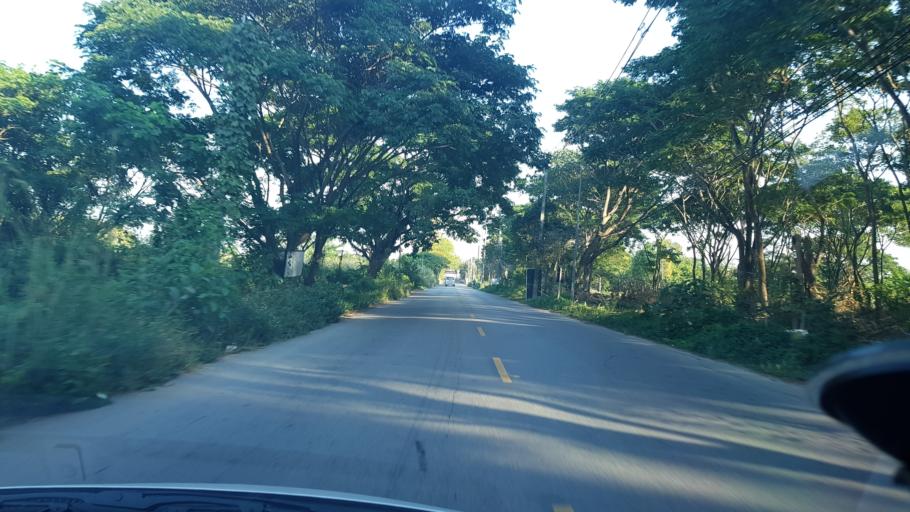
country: TH
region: Chiang Rai
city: Chiang Rai
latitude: 19.9302
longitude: 99.8254
